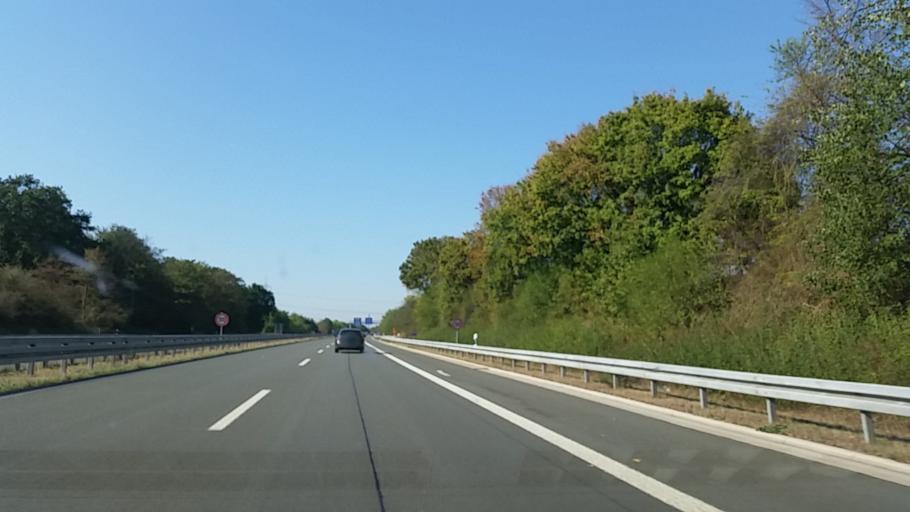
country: DE
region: North Rhine-Westphalia
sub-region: Regierungsbezirk Dusseldorf
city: Langenfeld
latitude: 51.0876
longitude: 6.9427
